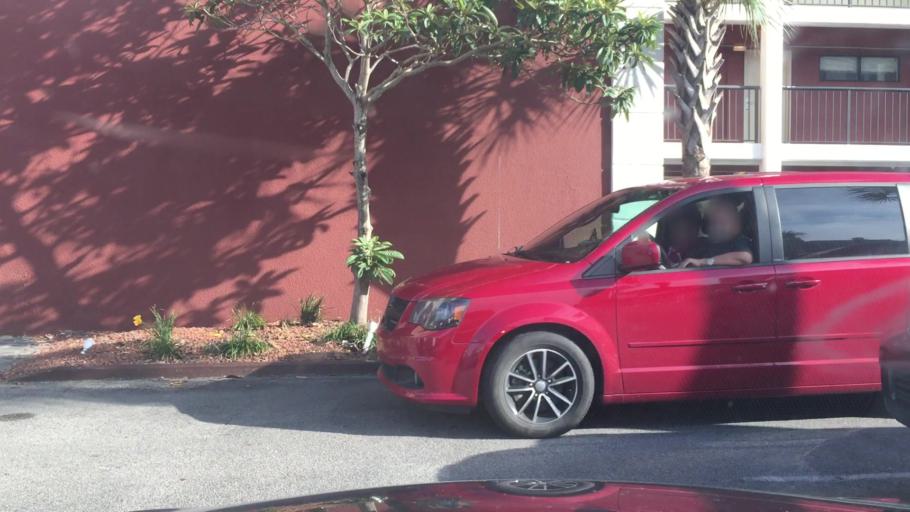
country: US
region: South Carolina
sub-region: Horry County
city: North Myrtle Beach
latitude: 33.8264
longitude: -78.6485
